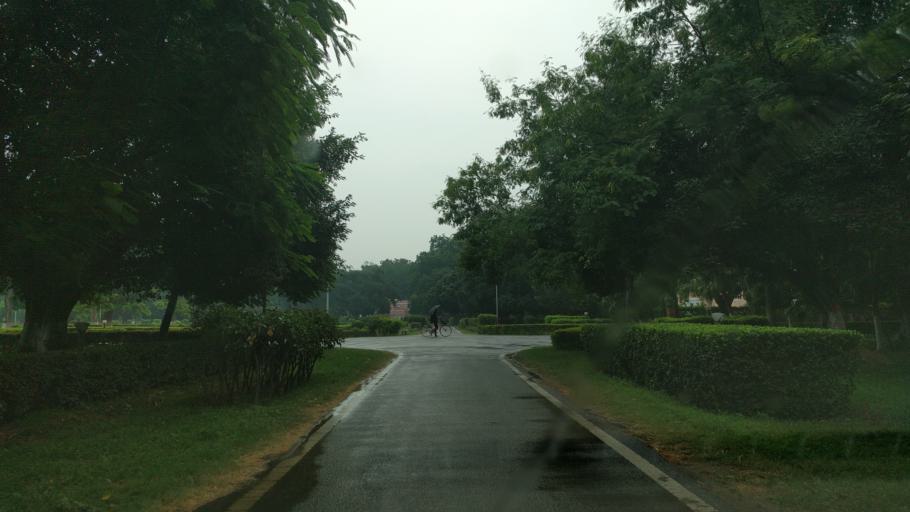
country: IN
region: NCT
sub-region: Central Delhi
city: Karol Bagh
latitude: 28.6388
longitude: 77.1657
